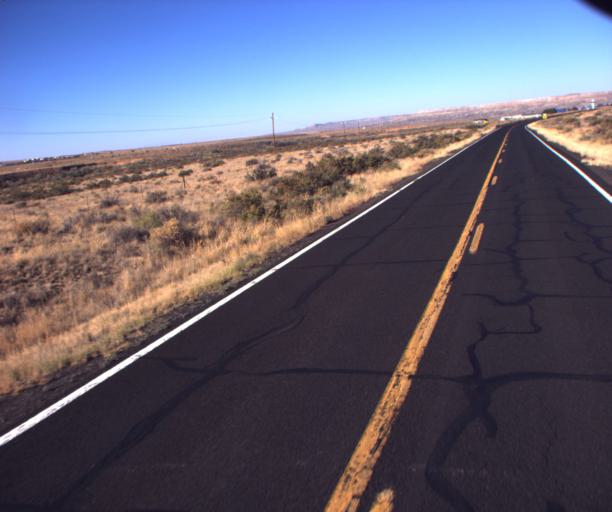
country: US
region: Arizona
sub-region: Navajo County
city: First Mesa
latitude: 35.8303
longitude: -110.2875
